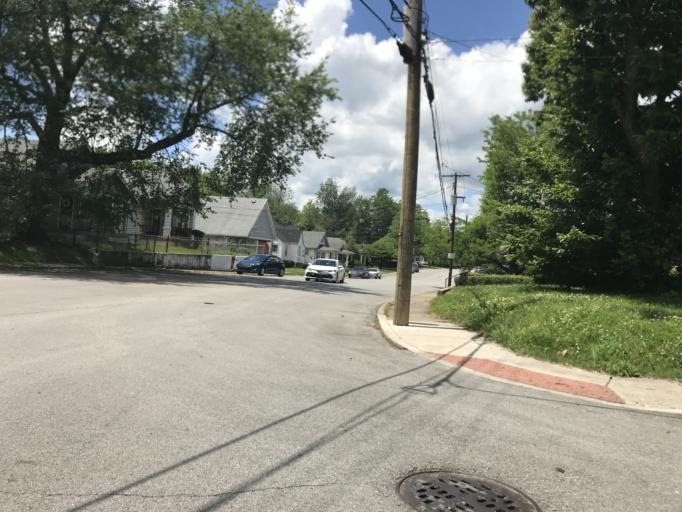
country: US
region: Kentucky
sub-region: Jefferson County
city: Shively
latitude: 38.2416
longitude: -85.8230
